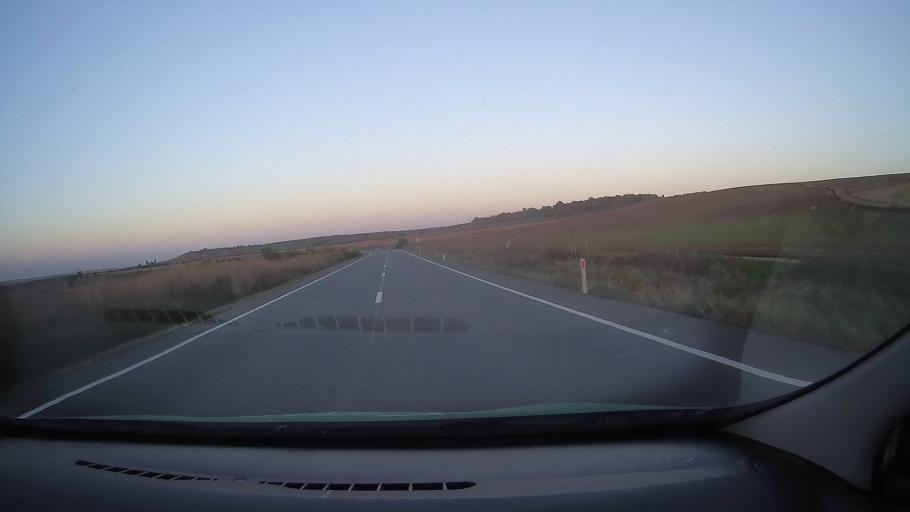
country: RO
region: Bihor
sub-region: Comuna Cherechiu
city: Cherechiu
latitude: 47.3945
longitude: 22.1558
